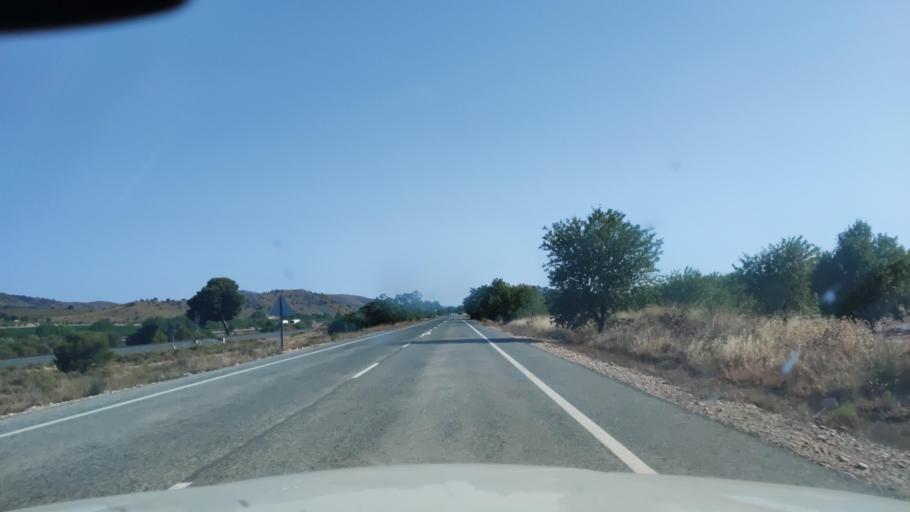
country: ES
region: Castille-La Mancha
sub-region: Provincia de Albacete
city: Tobarra
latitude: 38.6555
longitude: -1.6637
